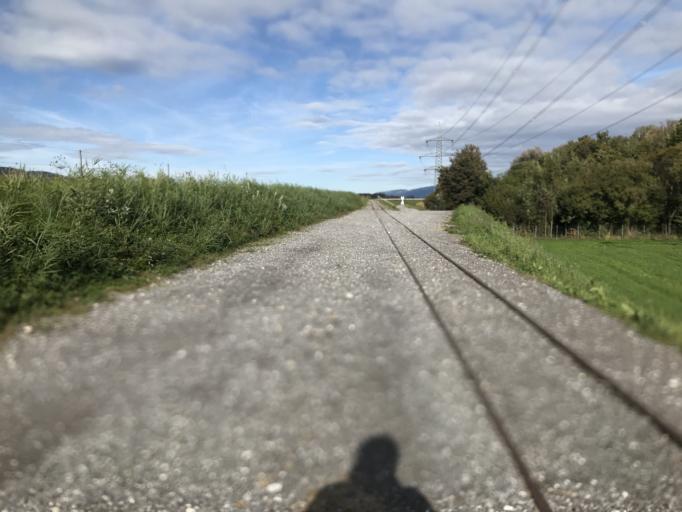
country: AT
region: Vorarlberg
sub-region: Politischer Bezirk Feldkirch
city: Mader
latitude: 47.3479
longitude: 9.6040
